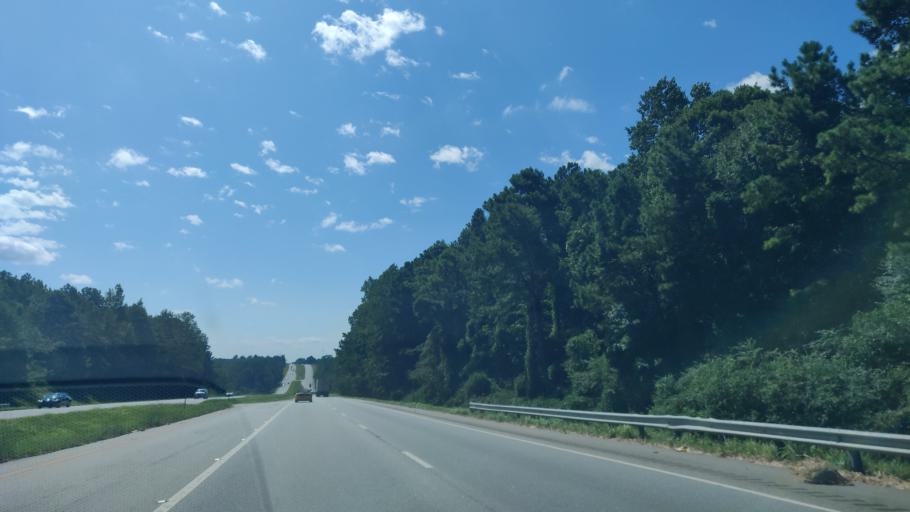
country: US
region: Alabama
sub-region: Lee County
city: Smiths Station
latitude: 32.5556
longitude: -85.1142
